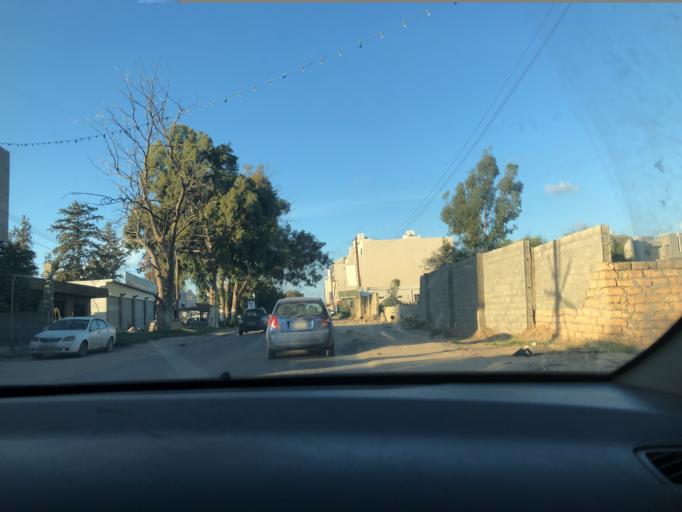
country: LY
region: Tripoli
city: Tagiura
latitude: 32.8565
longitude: 13.2789
